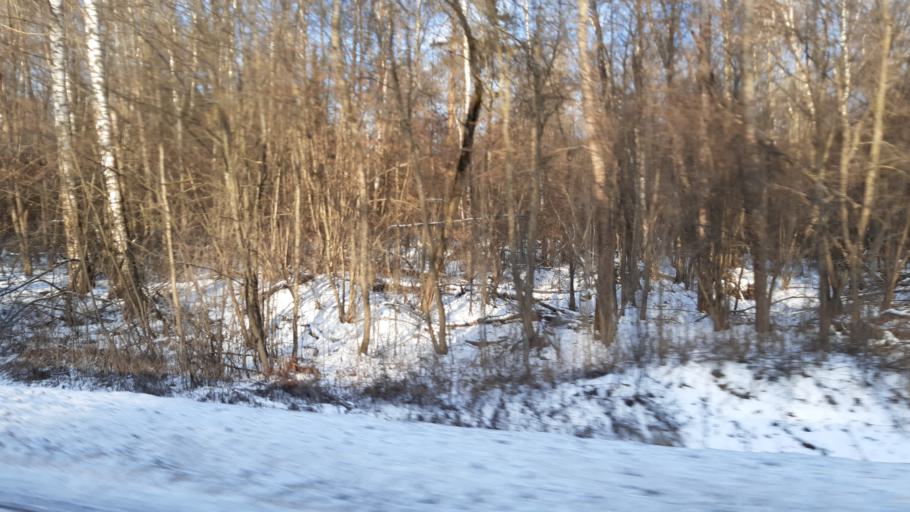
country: RU
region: Vladimir
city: Arsaki
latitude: 56.2914
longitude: 38.3803
